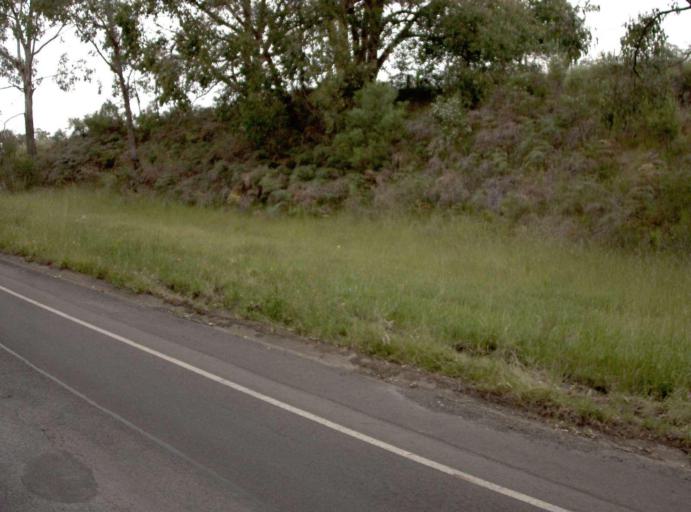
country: AU
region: Victoria
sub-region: Cardinia
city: Koo-Wee-Rup
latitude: -38.3399
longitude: 145.6288
